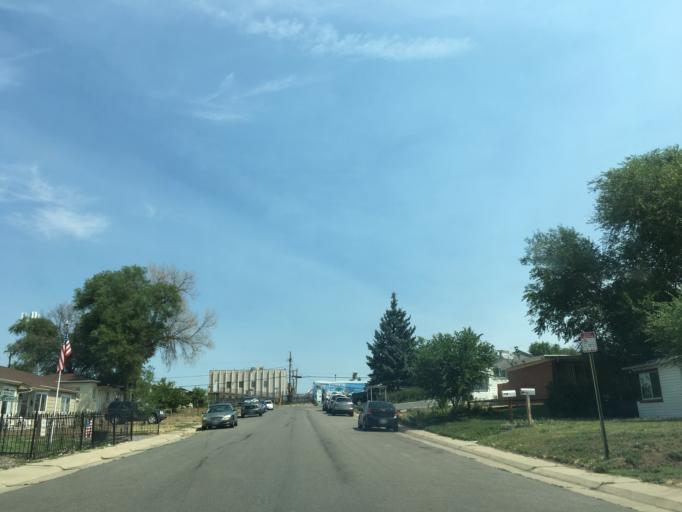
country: US
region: Colorado
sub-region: Jefferson County
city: Lakewood
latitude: 39.6957
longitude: -105.0519
